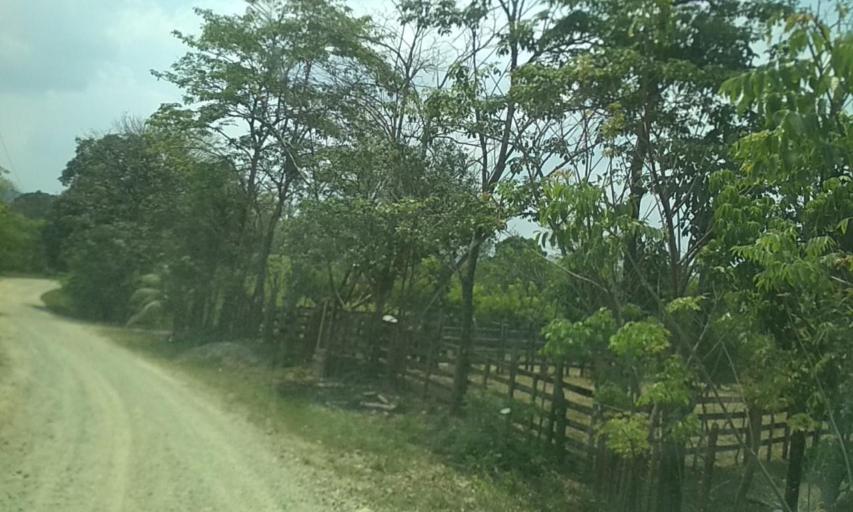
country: MX
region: Tabasco
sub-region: Huimanguillo
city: Francisco Rueda
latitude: 17.6065
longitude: -93.8066
